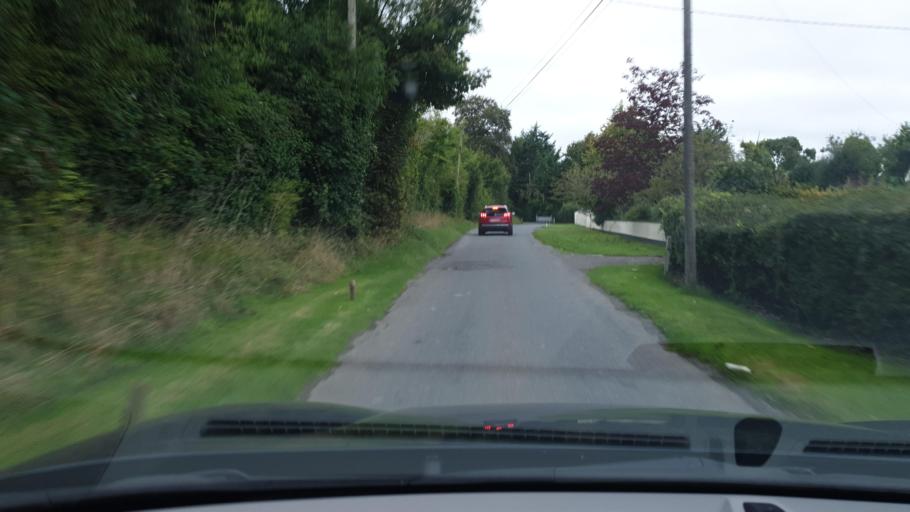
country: IE
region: Leinster
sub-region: An Mhi
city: Dunshaughlin
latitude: 53.5241
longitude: -6.5095
